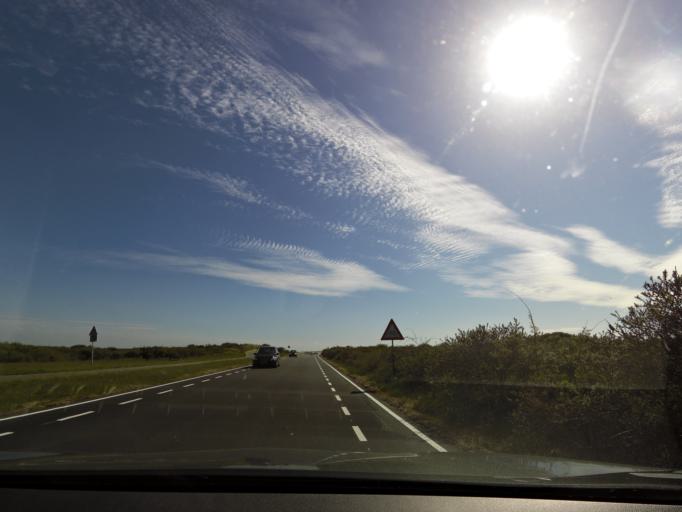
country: NL
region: Zeeland
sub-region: Schouwen-Duiveland
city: Scharendijke
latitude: 51.7810
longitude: 3.8673
